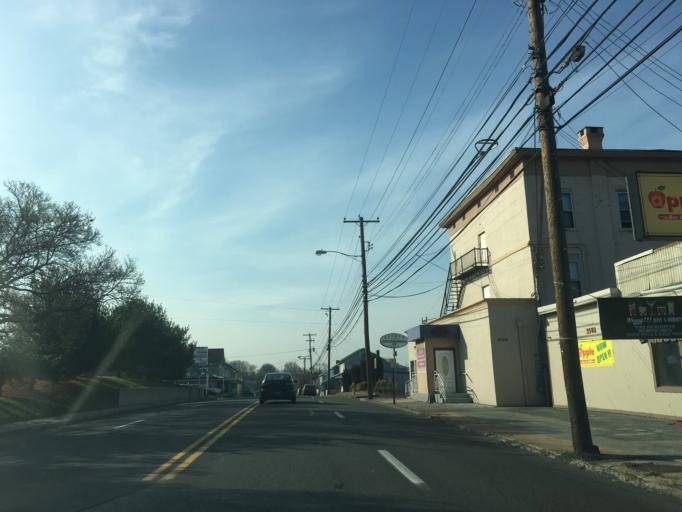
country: US
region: Pennsylvania
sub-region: Dauphin County
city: Progress
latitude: 40.2870
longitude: -76.8390
